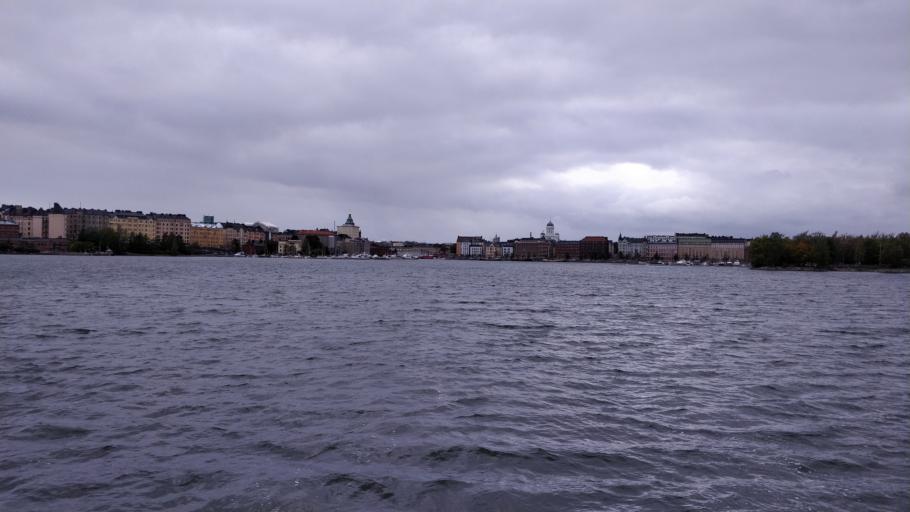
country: FI
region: Uusimaa
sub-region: Helsinki
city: Helsinki
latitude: 60.1724
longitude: 24.9765
